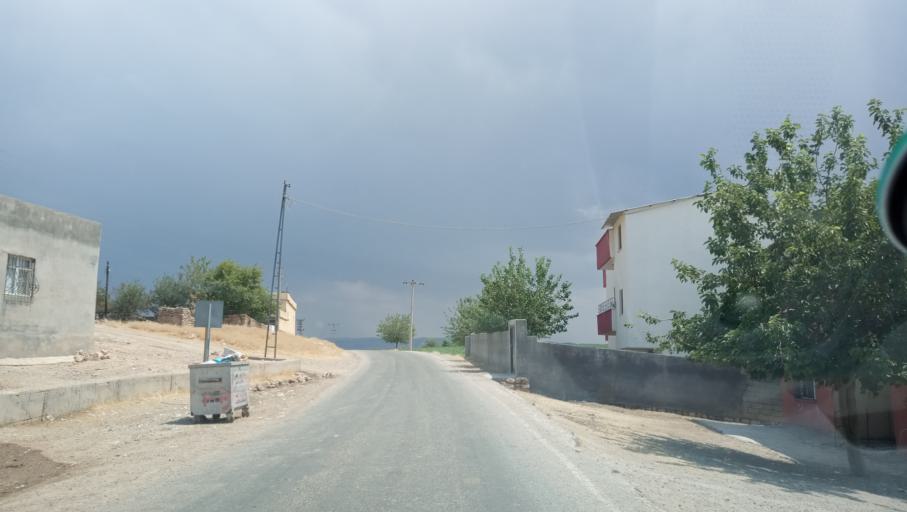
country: TR
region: Mardin
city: Baskavak
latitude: 37.6797
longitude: 40.8481
